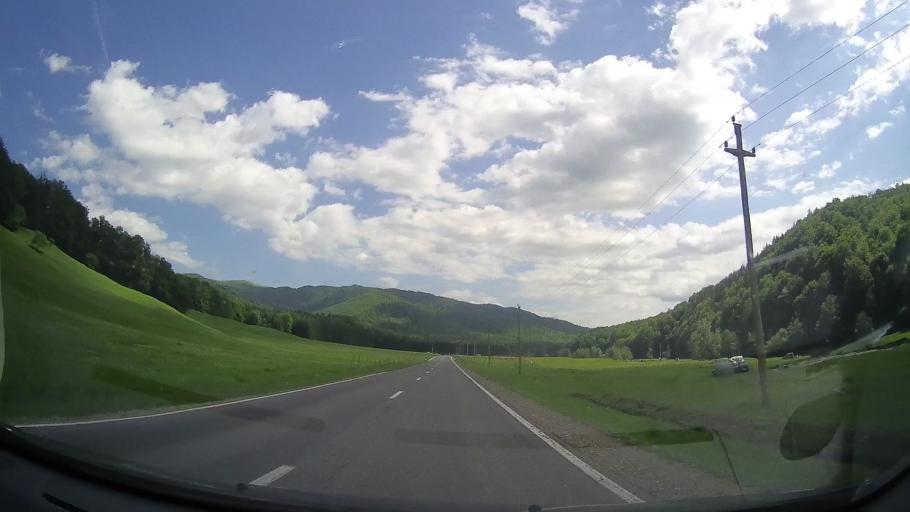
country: RO
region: Prahova
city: Maneciu
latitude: 45.4251
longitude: 25.9411
